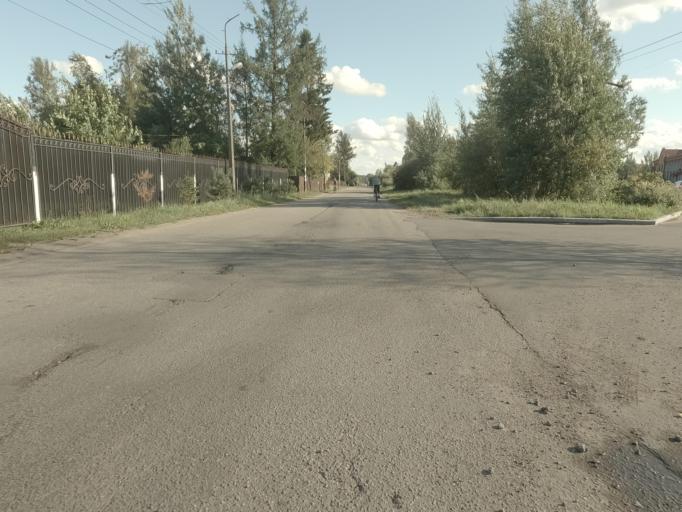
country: RU
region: Leningrad
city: Imeni Morozova
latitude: 59.9624
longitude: 31.0301
